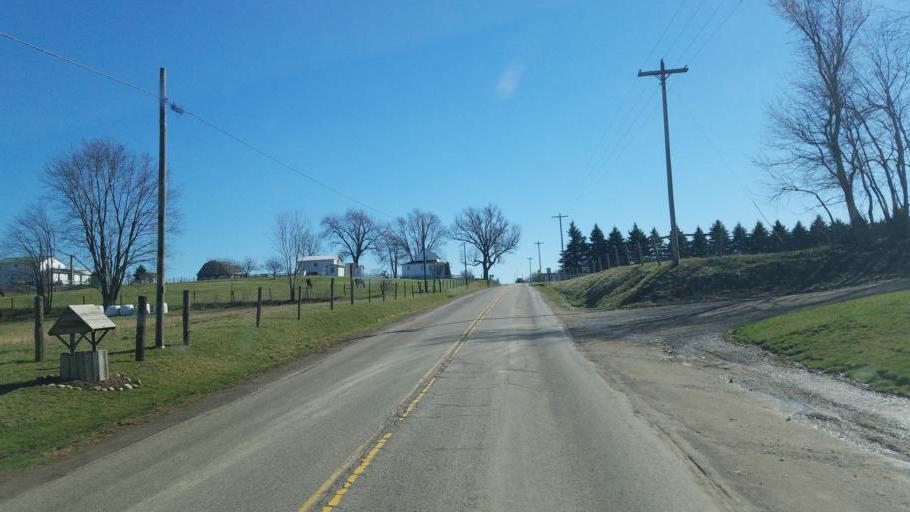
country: US
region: Ohio
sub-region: Wayne County
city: Apple Creek
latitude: 40.6971
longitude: -81.7872
